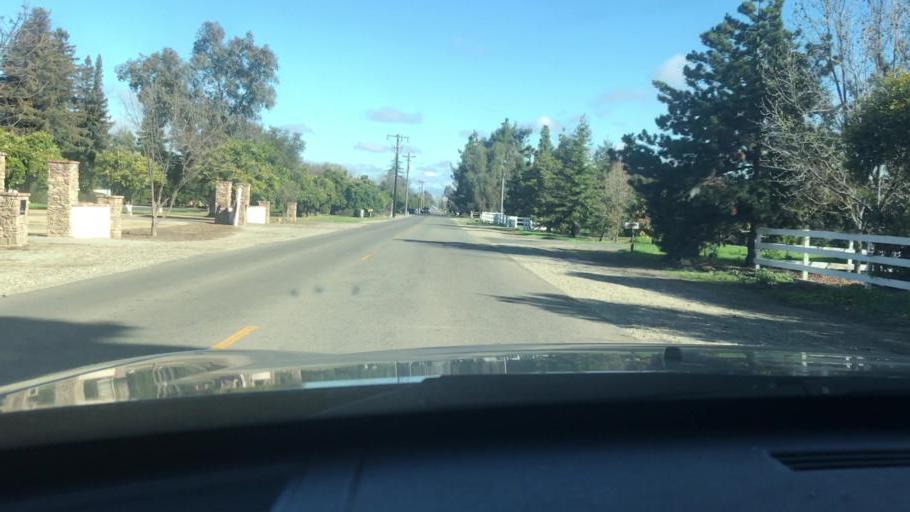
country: US
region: California
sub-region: Fresno County
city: Clovis
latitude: 36.8687
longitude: -119.6840
